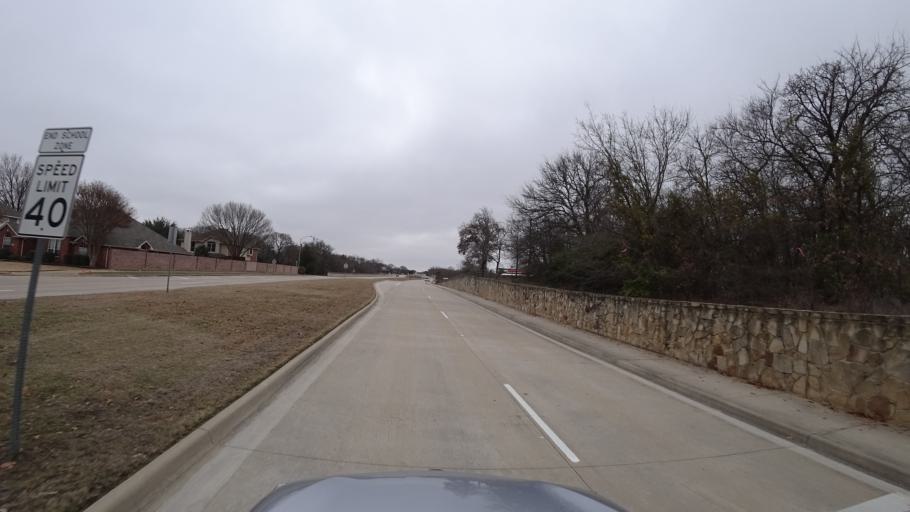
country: US
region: Texas
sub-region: Denton County
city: Lewisville
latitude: 33.0291
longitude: -97.0363
